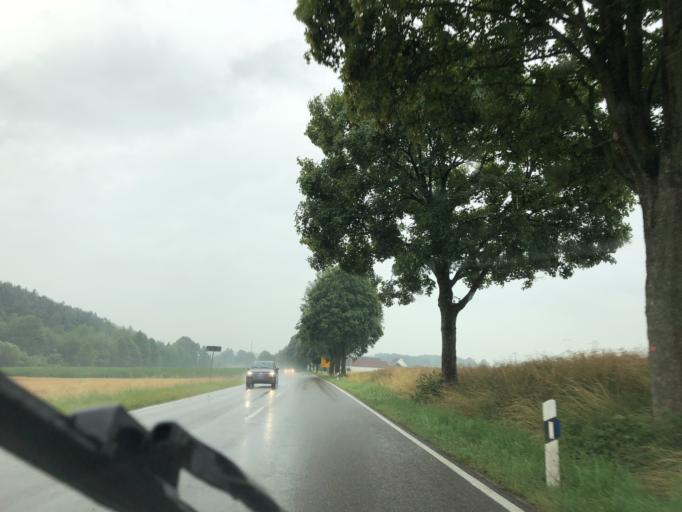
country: DE
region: Bavaria
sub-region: Upper Bavaria
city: Attenkirchen
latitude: 48.4842
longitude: 11.7596
